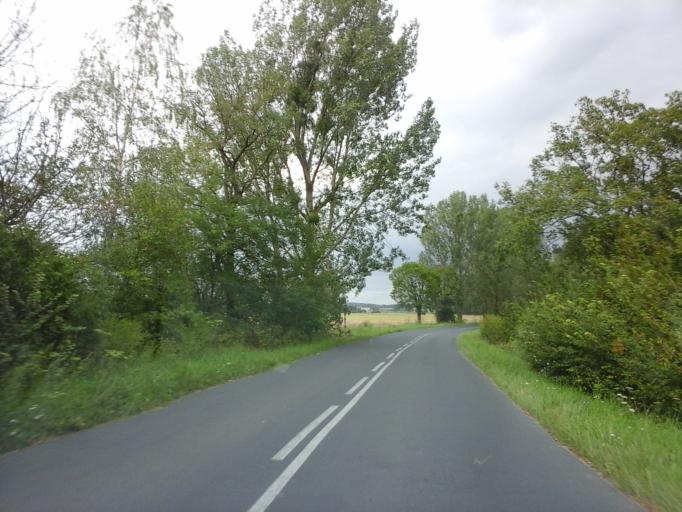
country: PL
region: West Pomeranian Voivodeship
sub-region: Powiat choszczenski
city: Krzecin
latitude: 53.1226
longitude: 15.4522
